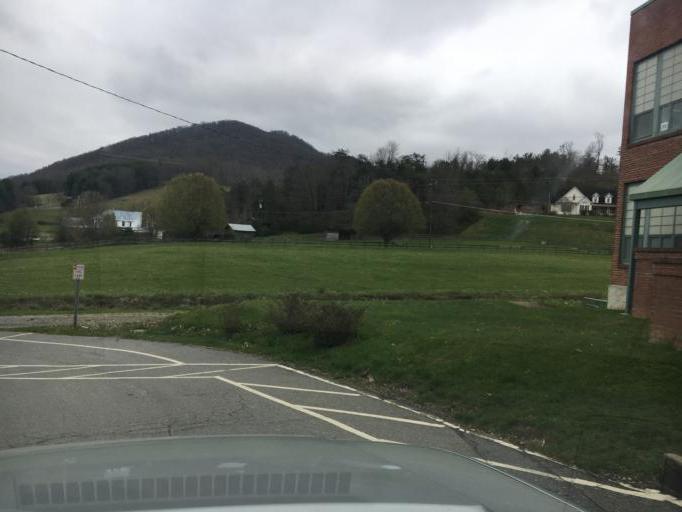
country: US
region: North Carolina
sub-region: Madison County
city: Mars Hill
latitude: 35.7751
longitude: -82.4595
